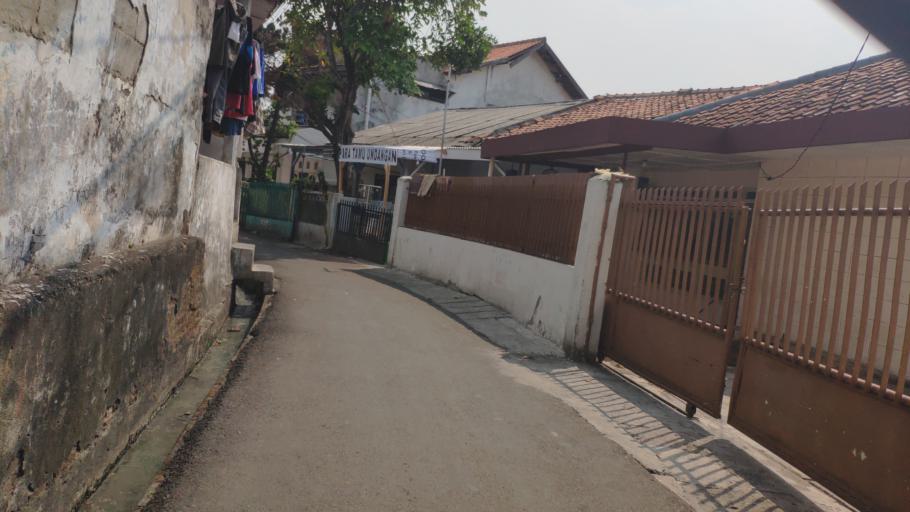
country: ID
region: Jakarta Raya
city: Jakarta
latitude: -6.2547
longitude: 106.7934
